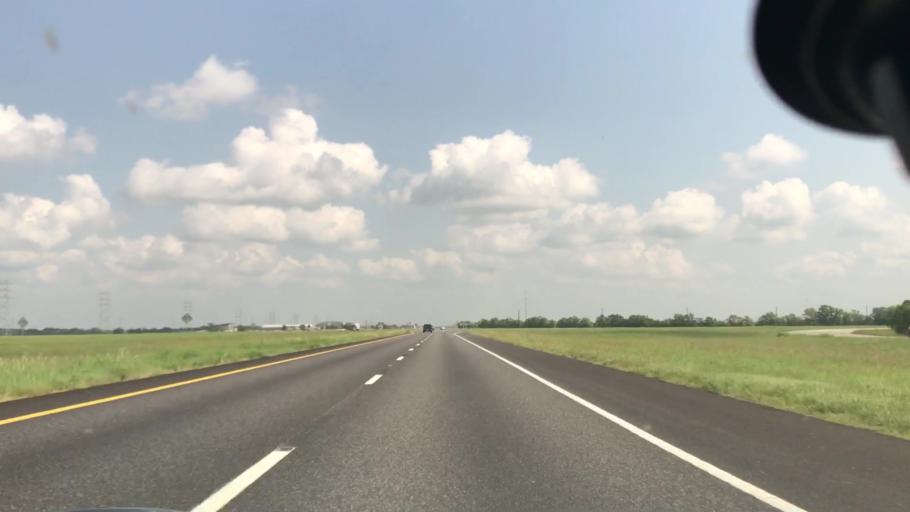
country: US
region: Texas
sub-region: Brazoria County
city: Rosharon
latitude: 29.4076
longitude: -95.4268
